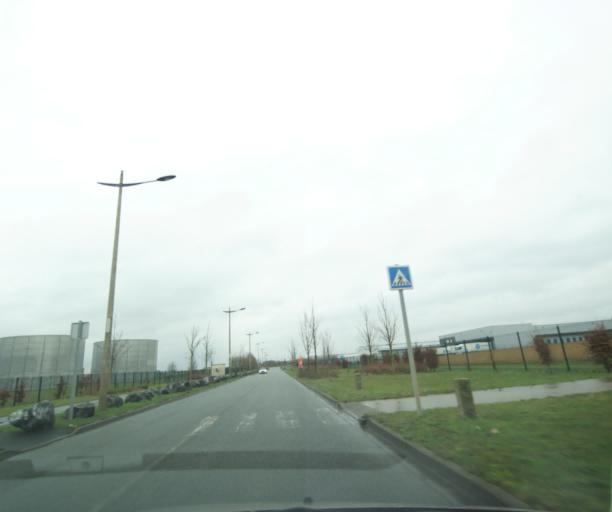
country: FR
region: Nord-Pas-de-Calais
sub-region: Departement du Nord
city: Haulchin
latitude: 50.3333
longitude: 3.4398
